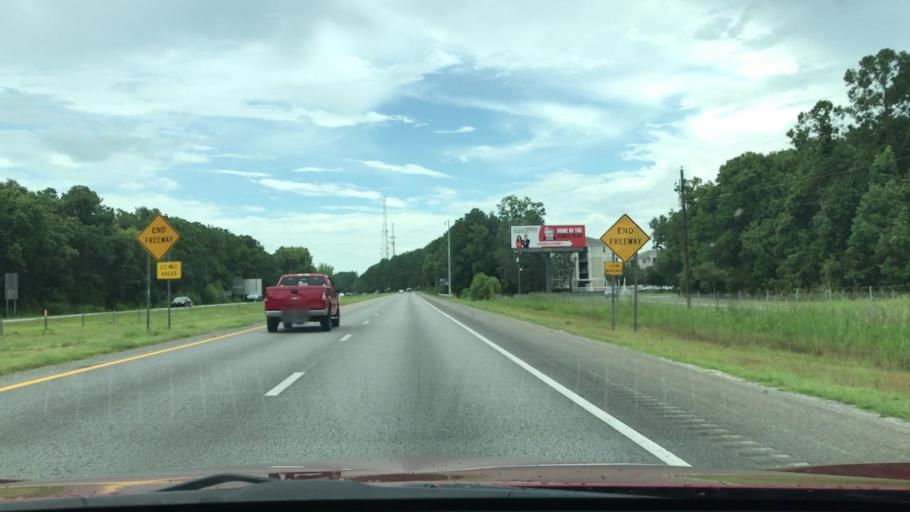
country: US
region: South Carolina
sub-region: Charleston County
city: Shell Point
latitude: 32.8013
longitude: -80.0361
